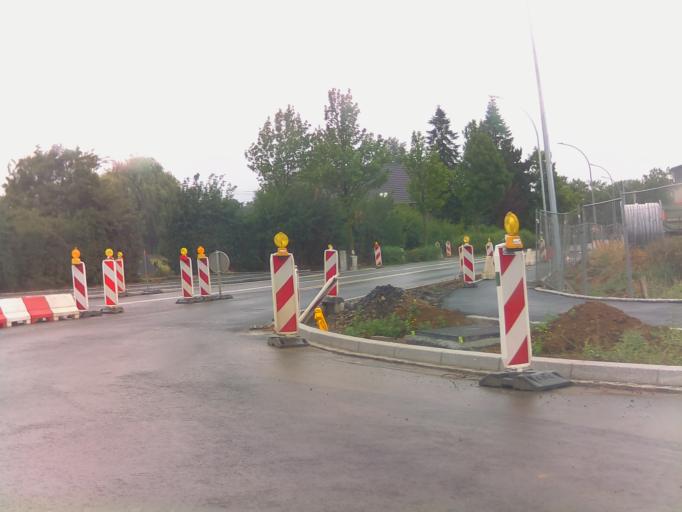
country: LU
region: Luxembourg
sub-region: Canton d'Esch-sur-Alzette
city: Sanem
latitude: 49.5390
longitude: 5.9378
